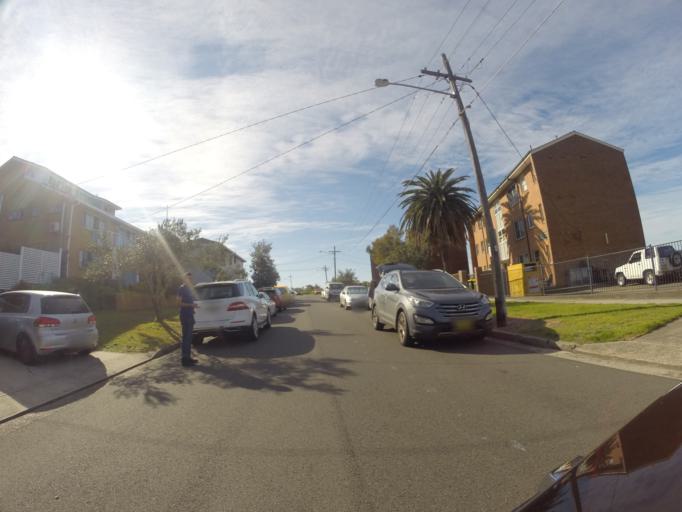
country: AU
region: New South Wales
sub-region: Randwick
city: South Coogee
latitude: -33.9359
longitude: 151.2565
